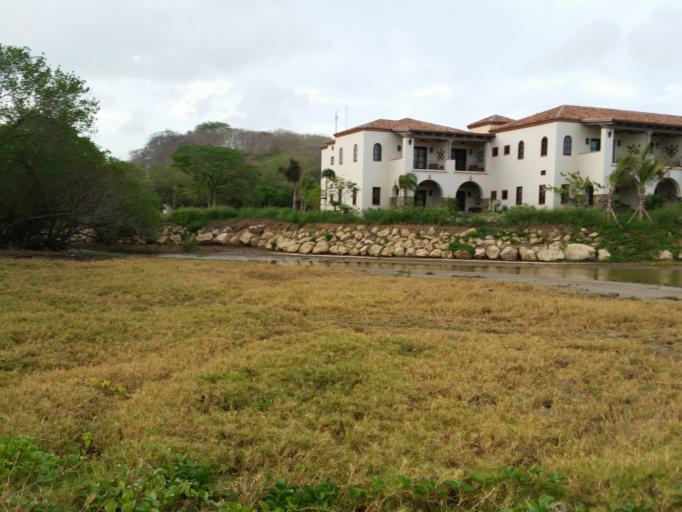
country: NI
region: Rivas
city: Tola
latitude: 11.4426
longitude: -86.0858
